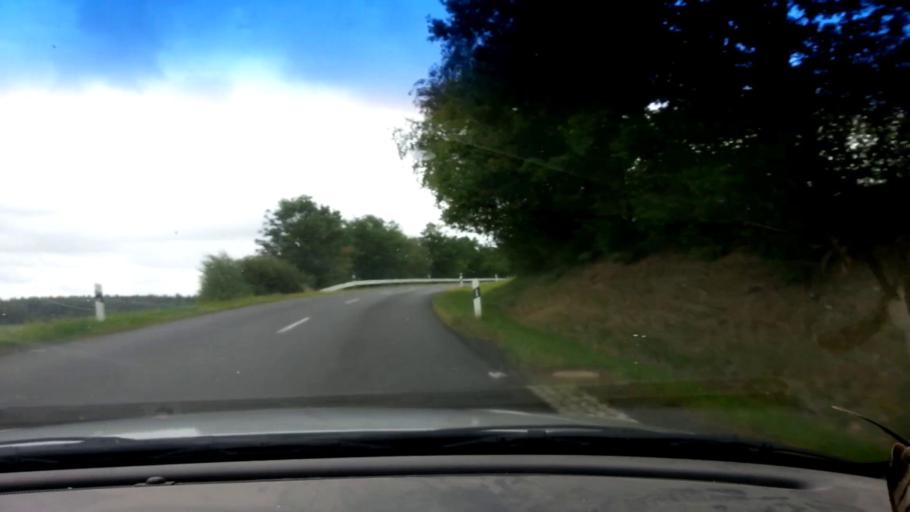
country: DE
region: Bavaria
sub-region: Upper Palatinate
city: Waldsassen
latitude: 50.0330
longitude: 12.2819
